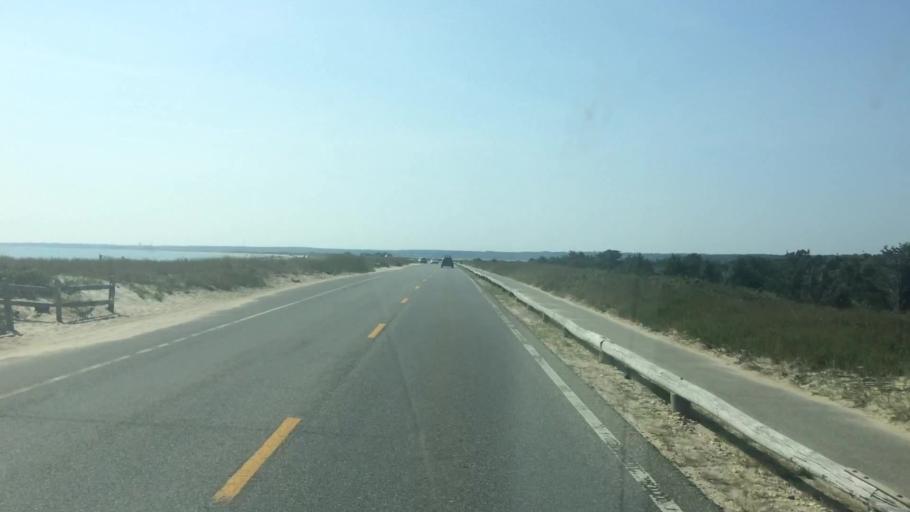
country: US
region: Massachusetts
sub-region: Dukes County
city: Oak Bluffs
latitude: 41.4314
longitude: -70.5563
